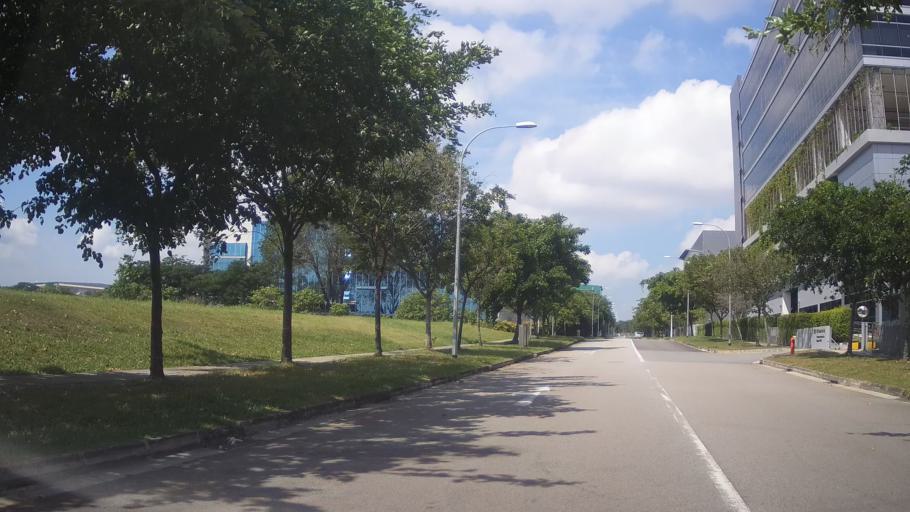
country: SG
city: Singapore
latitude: 1.3241
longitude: 103.7165
